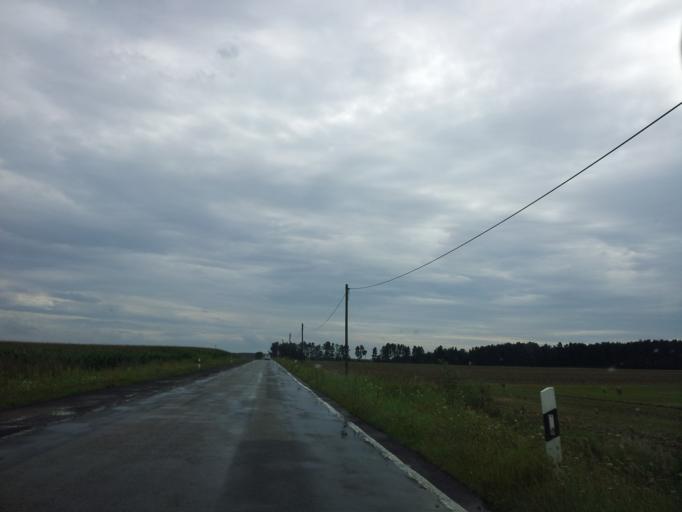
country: DE
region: Brandenburg
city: Gorzke
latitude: 52.1905
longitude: 12.3836
